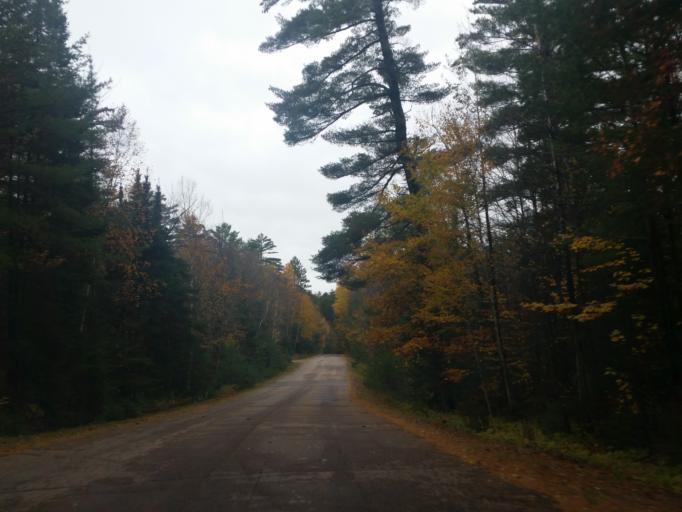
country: CA
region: Ontario
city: Deep River
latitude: 45.9923
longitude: -77.4022
